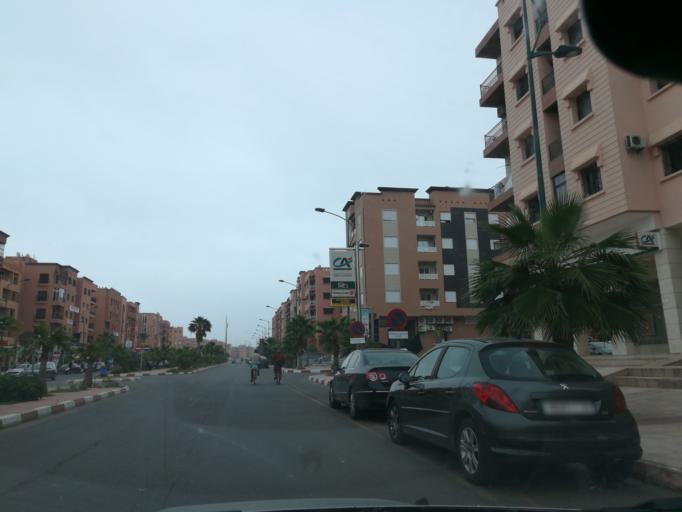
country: MA
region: Marrakech-Tensift-Al Haouz
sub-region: Marrakech
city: Marrakesh
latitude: 31.6733
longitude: -8.0207
